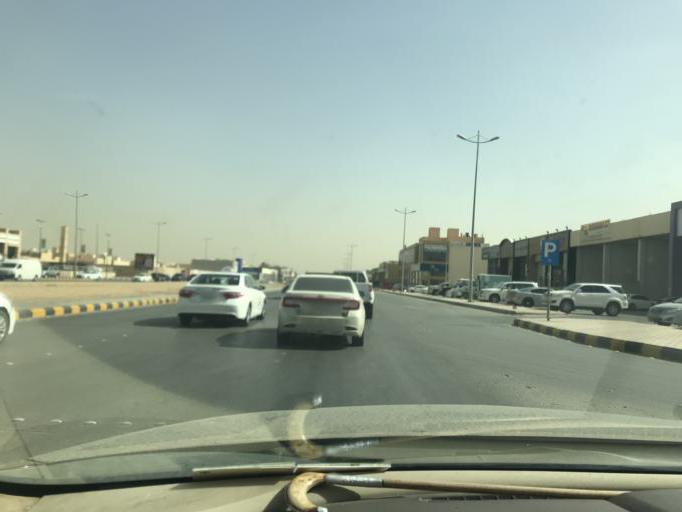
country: SA
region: Ar Riyad
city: Riyadh
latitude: 24.8075
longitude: 46.7364
